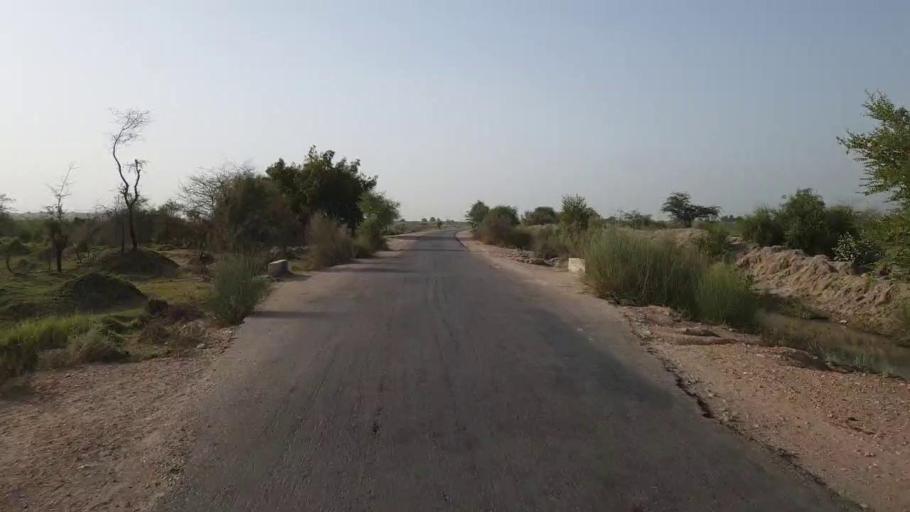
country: PK
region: Sindh
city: Jam Sahib
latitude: 26.4592
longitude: 68.8591
